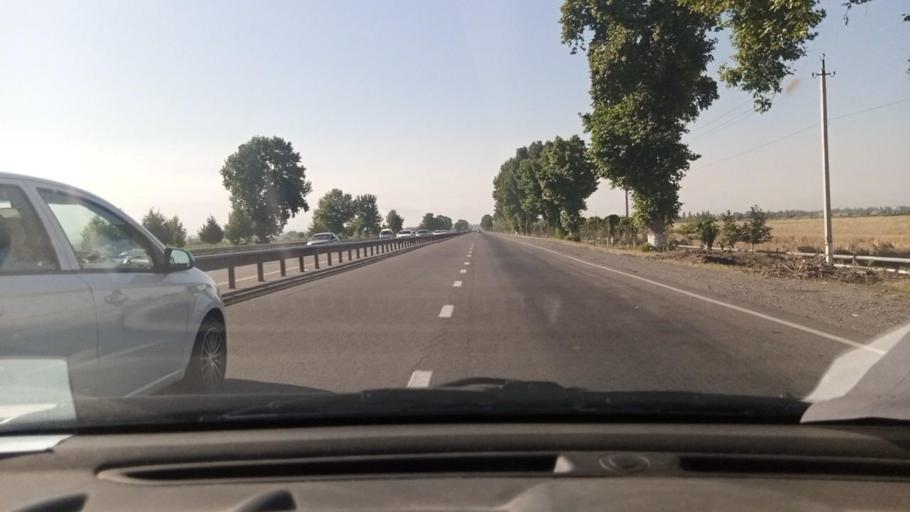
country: UZ
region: Toshkent Shahri
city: Bektemir
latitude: 41.1676
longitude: 69.4159
